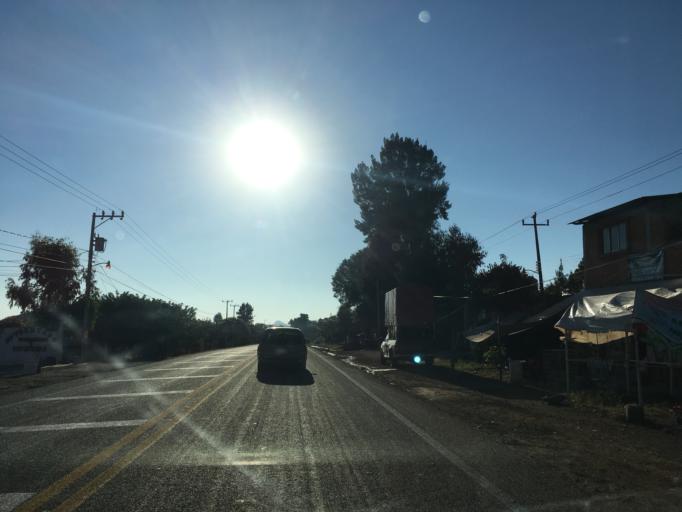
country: MX
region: Michoacan
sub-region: Zitacuaro
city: Puentecillas (Tercera Manzana de Zirahuato)
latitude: 19.4842
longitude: -100.4196
